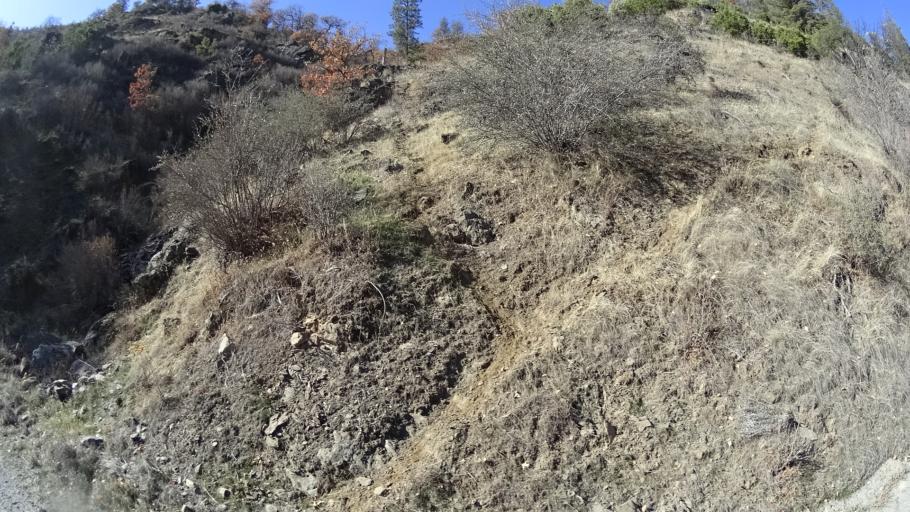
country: US
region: California
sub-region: Siskiyou County
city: Yreka
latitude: 41.8433
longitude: -122.6846
